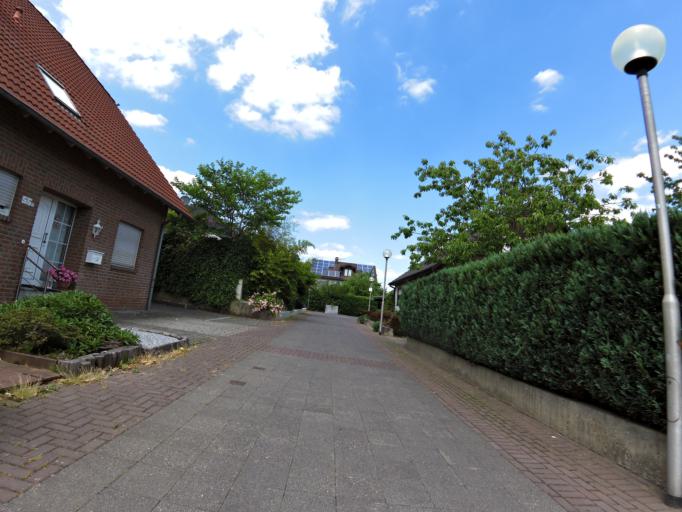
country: DE
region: North Rhine-Westphalia
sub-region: Regierungsbezirk Koln
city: Herzogenrath
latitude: 50.8626
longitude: 6.0916
